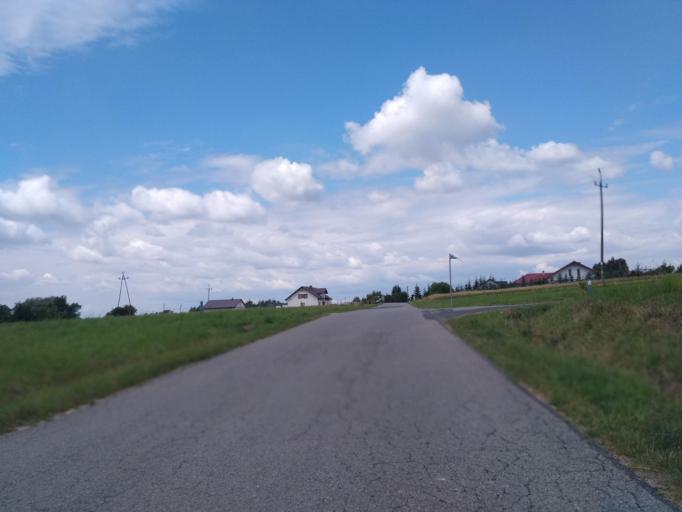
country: PL
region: Subcarpathian Voivodeship
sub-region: Powiat rzeszowski
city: Hyzne
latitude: 49.9149
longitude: 22.2148
